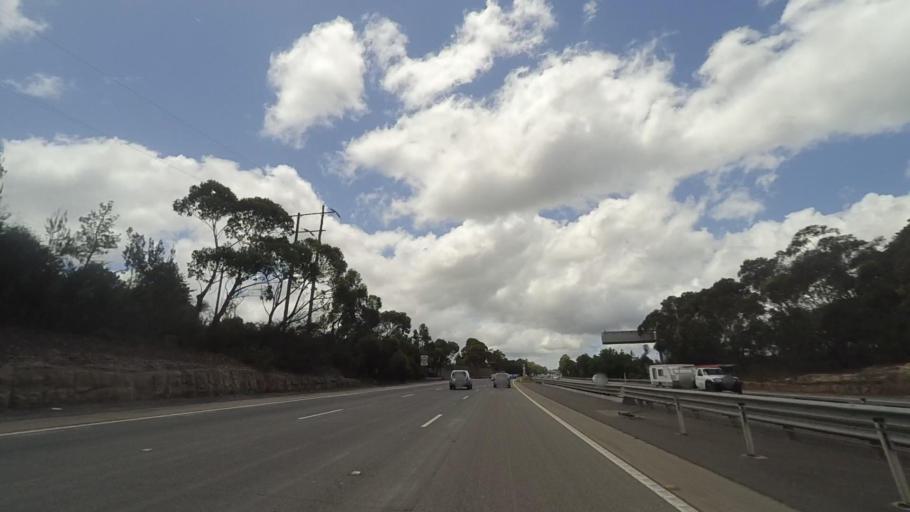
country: AU
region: New South Wales
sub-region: Hornsby Shire
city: Mount Colah
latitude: -33.6625
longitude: 151.1262
